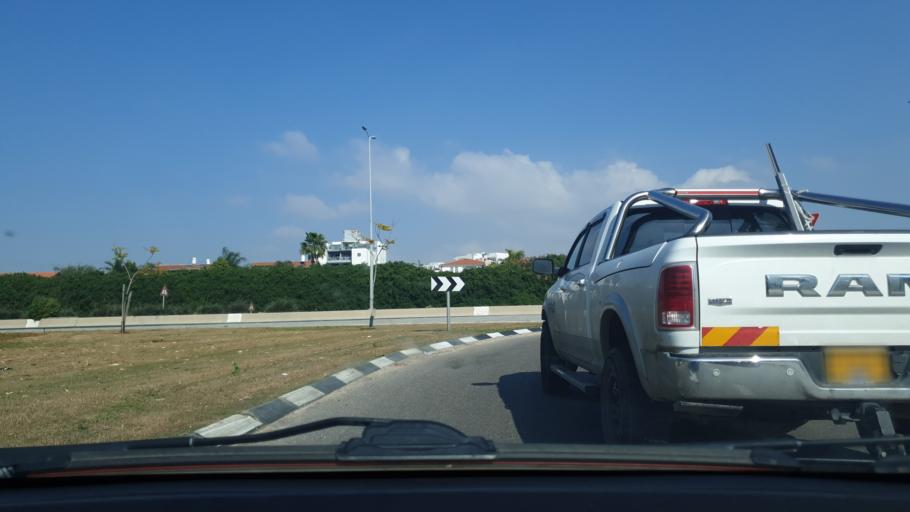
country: IL
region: Tel Aviv
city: Azor
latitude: 32.0156
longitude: 34.8100
